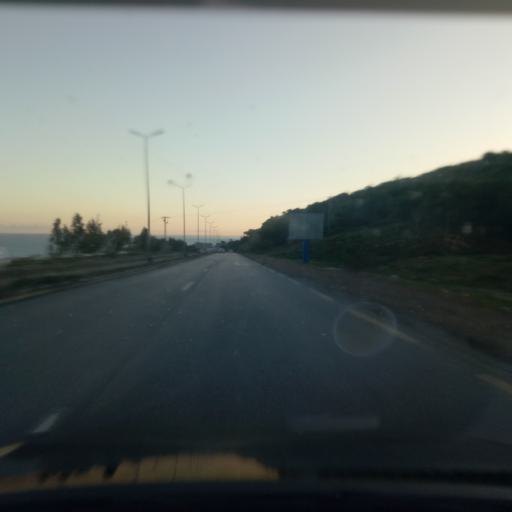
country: DZ
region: Tipaza
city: Bou Ismail
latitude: 36.6534
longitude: 2.7167
